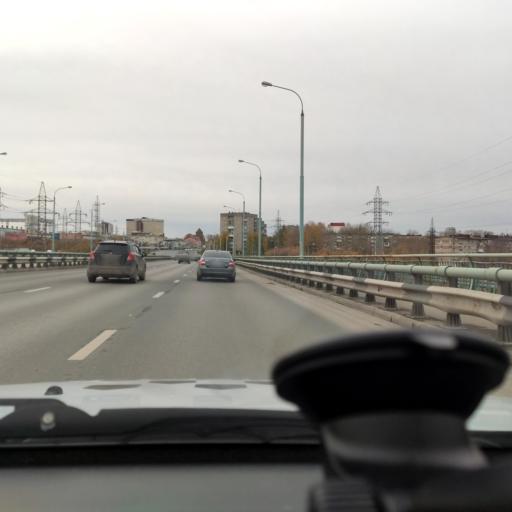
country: RU
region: Perm
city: Perm
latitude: 57.9870
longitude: 56.2757
